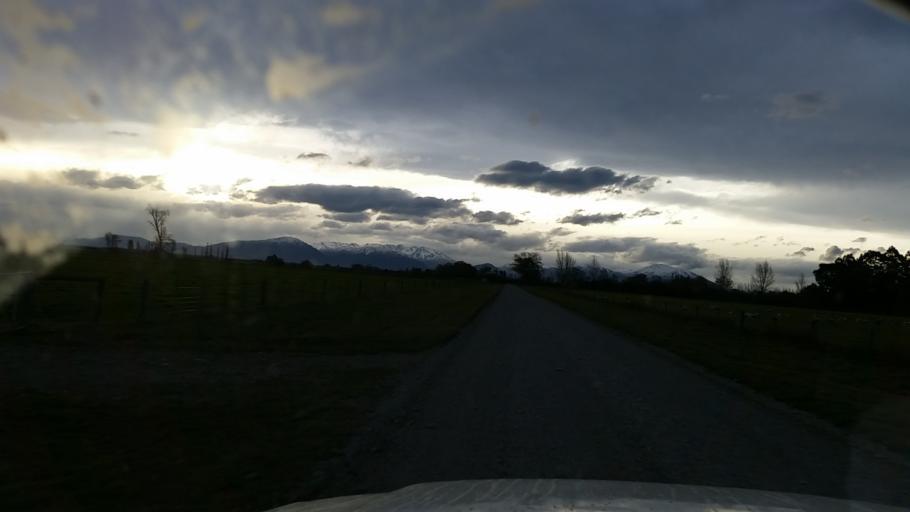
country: NZ
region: Canterbury
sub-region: Ashburton District
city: Ashburton
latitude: -43.8410
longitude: 171.6574
